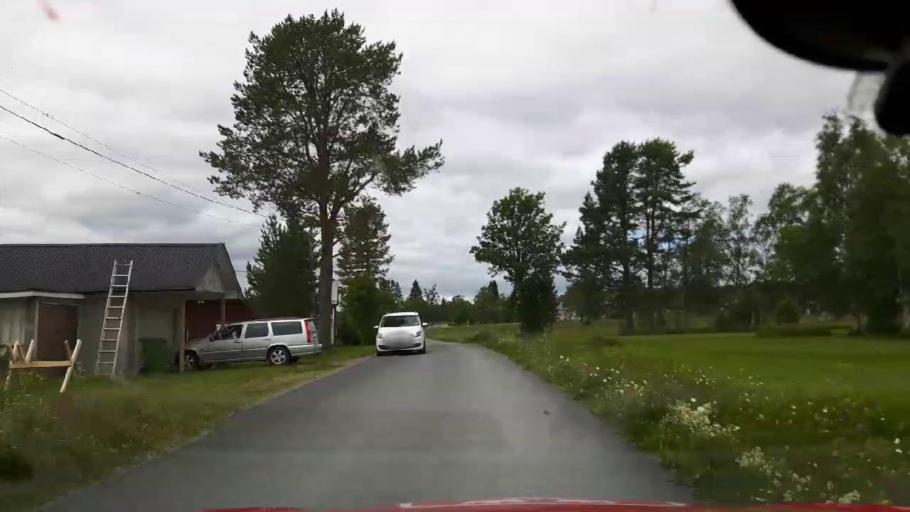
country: SE
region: Jaemtland
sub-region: OEstersunds Kommun
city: Brunflo
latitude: 63.0706
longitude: 14.8919
